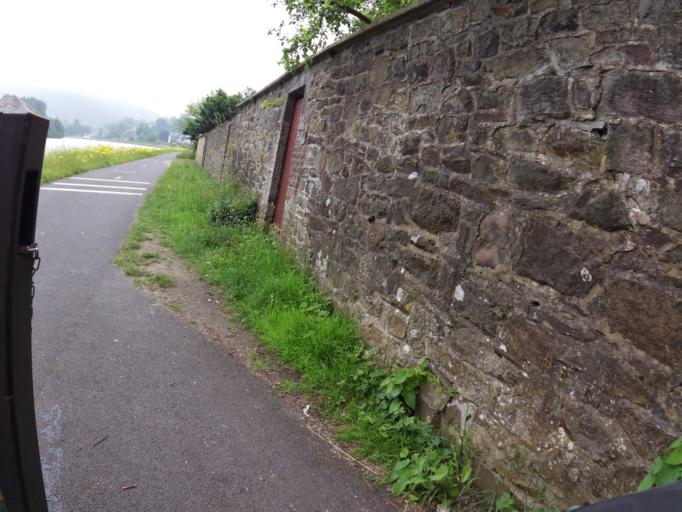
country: FR
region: Champagne-Ardenne
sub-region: Departement des Ardennes
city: Haybes
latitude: 50.0108
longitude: 4.7099
